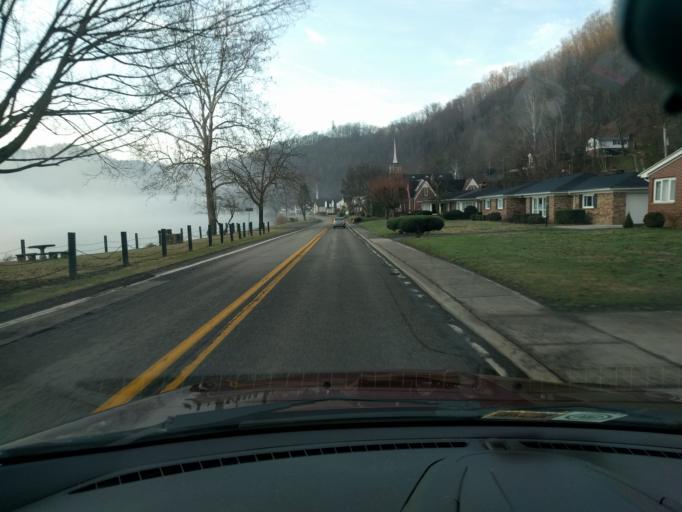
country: US
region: West Virginia
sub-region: Kanawha County
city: Montgomery
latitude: 38.1557
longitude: -81.2146
